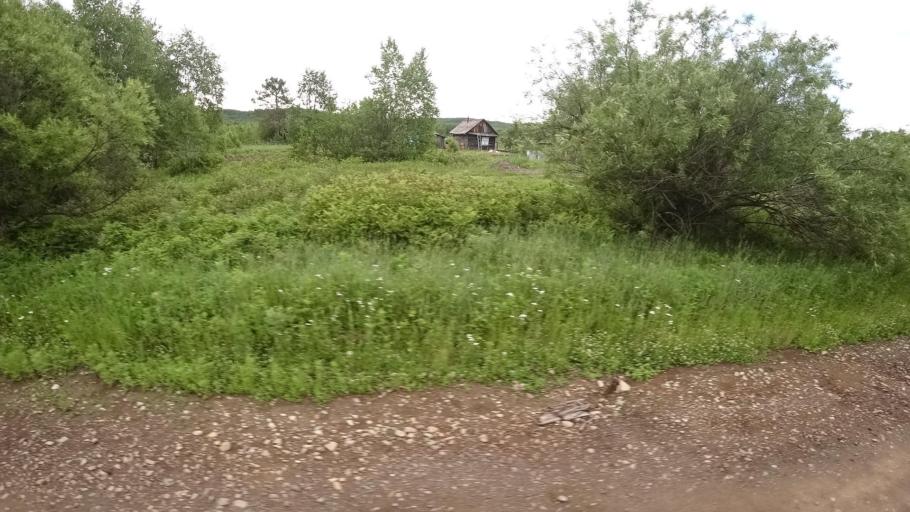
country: RU
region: Khabarovsk Krai
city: Amursk
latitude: 49.9149
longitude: 136.1607
